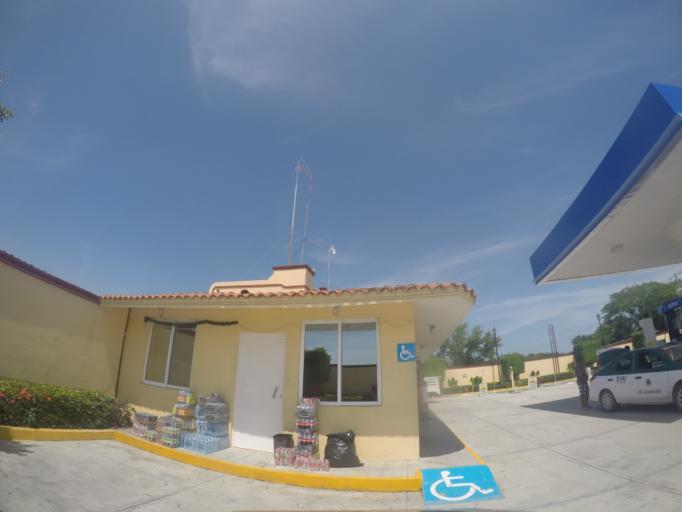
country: MX
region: Oaxaca
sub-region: Villa de Tututepec de Melchor Ocampo
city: Santa Rosa de Lima
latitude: 16.0111
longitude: -97.4516
